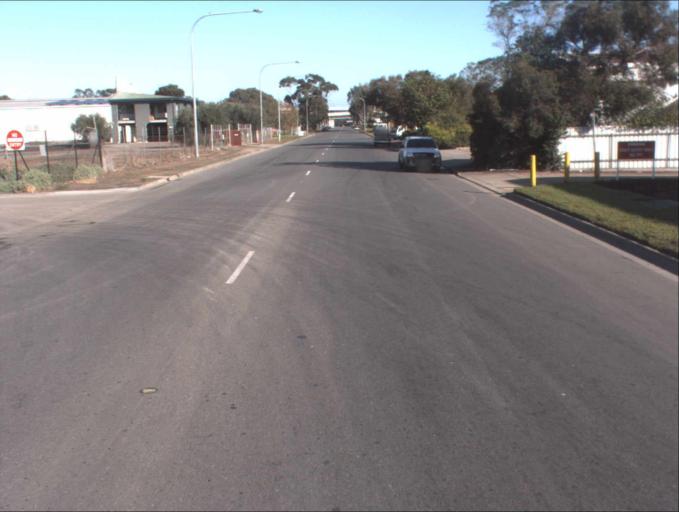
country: AU
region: South Australia
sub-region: Port Adelaide Enfield
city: Blair Athol
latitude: -34.8467
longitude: 138.5716
